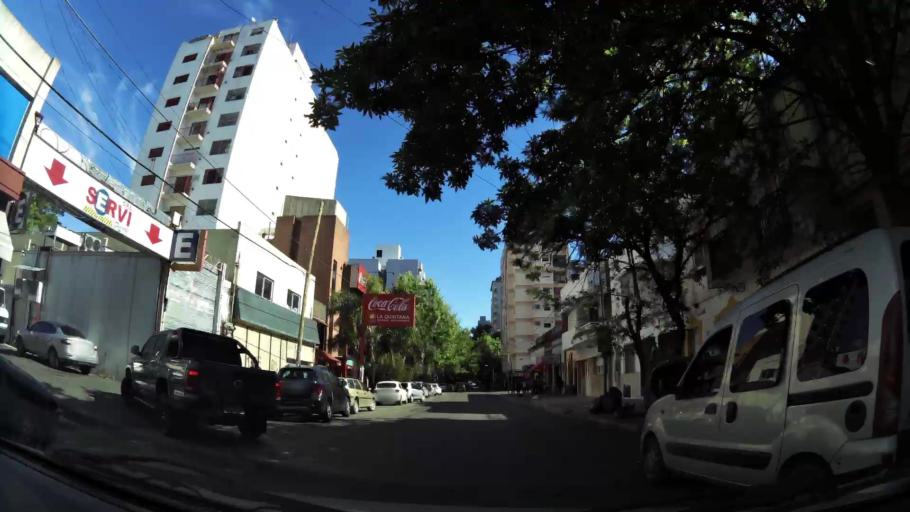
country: AR
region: Buenos Aires
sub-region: Partido de Lomas de Zamora
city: Lomas de Zamora
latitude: -34.7597
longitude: -58.4039
